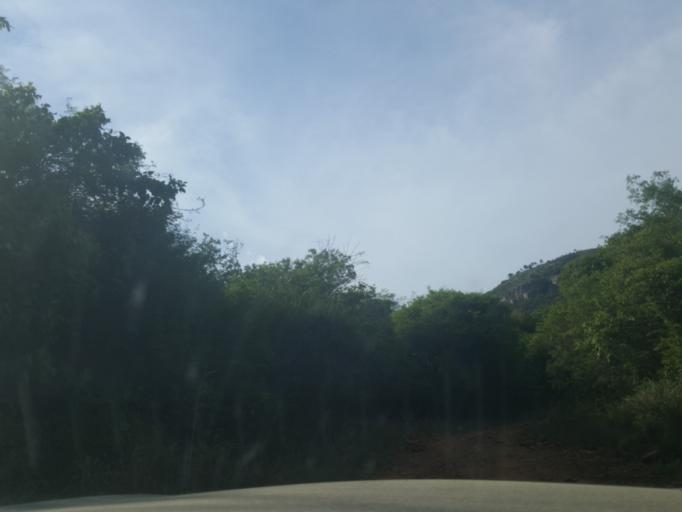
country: ZA
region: Limpopo
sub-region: Mopani District Municipality
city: Hoedspruit
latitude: -24.5912
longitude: 30.8285
